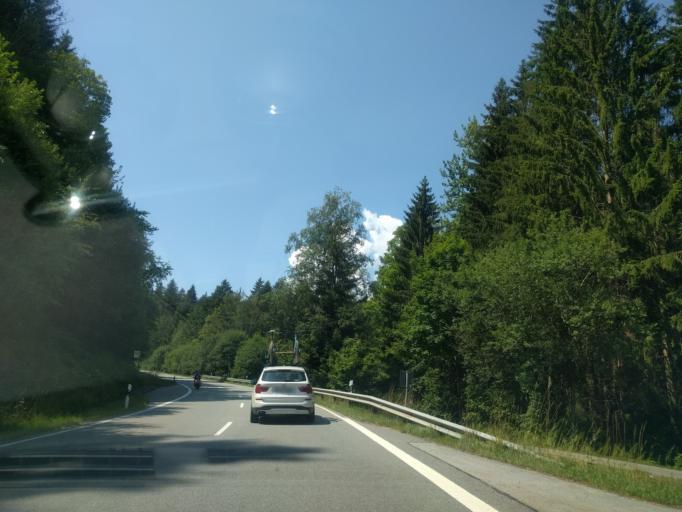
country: DE
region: Bavaria
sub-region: Lower Bavaria
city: Innernzell
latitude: 48.8583
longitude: 13.3029
